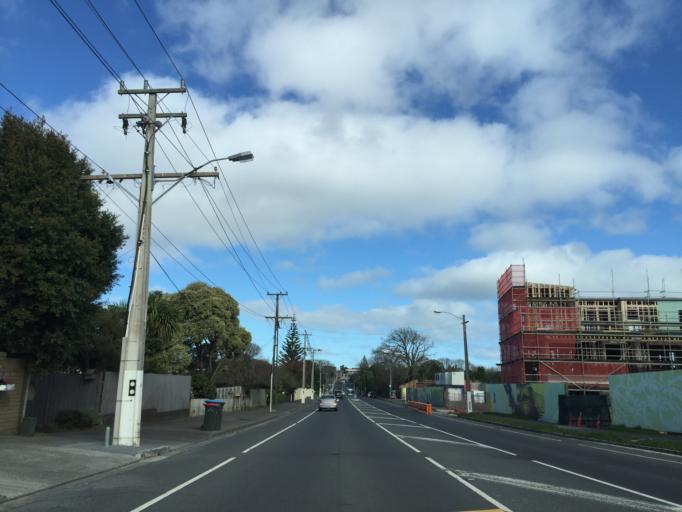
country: NZ
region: Auckland
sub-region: Auckland
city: Auckland
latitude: -36.9037
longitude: 174.7594
